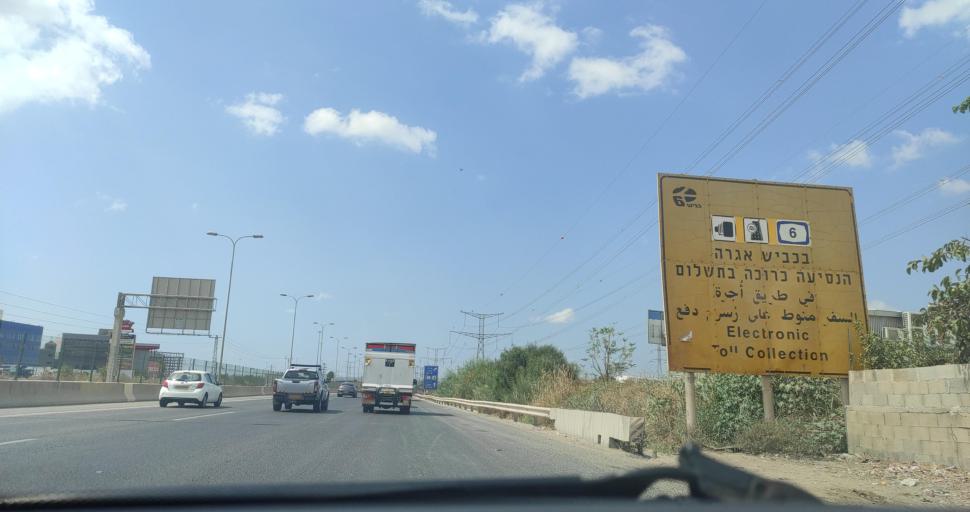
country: IL
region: Central District
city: Rosh Ha'Ayin
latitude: 32.1129
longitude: 34.9518
